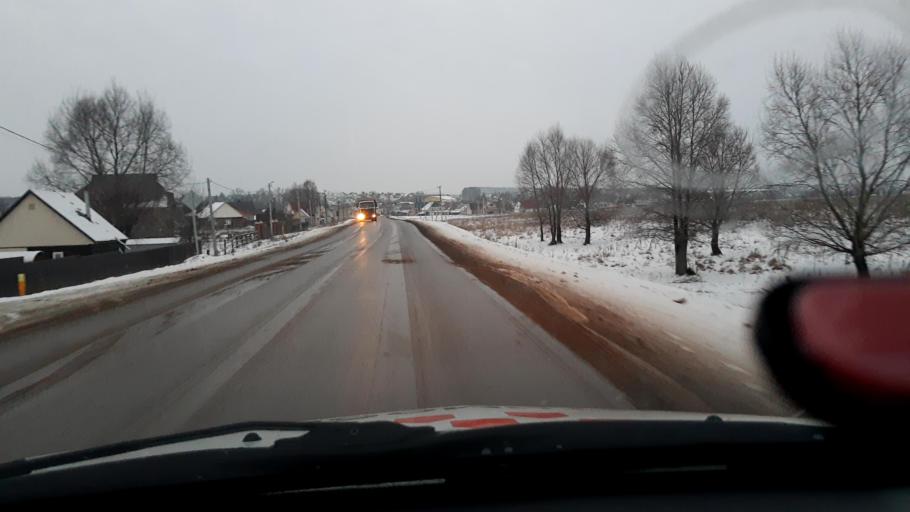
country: RU
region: Bashkortostan
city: Iglino
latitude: 54.8440
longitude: 56.4528
